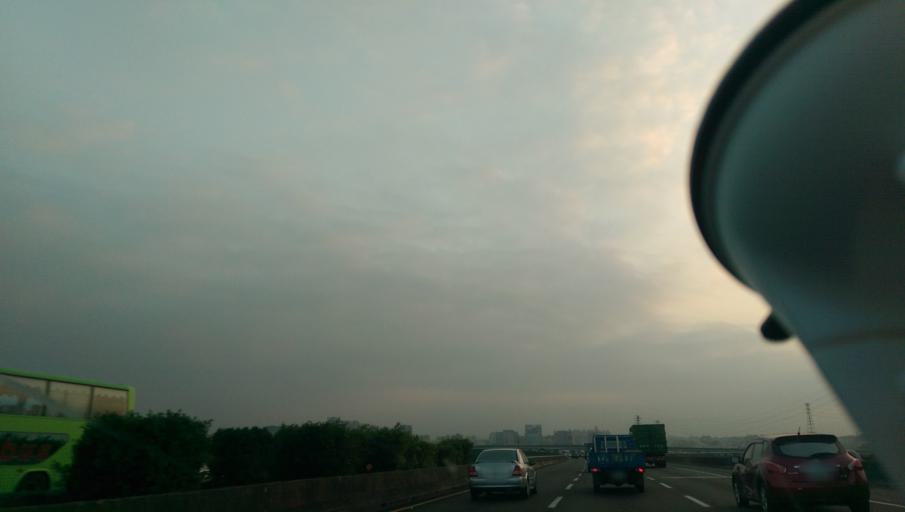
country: TW
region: Taiwan
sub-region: Hsinchu
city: Zhubei
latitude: 24.8177
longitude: 121.0136
